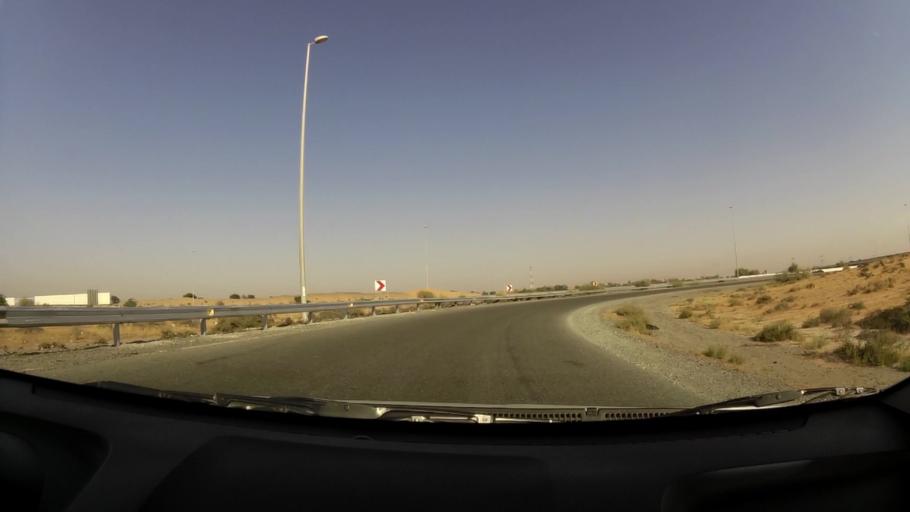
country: AE
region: Umm al Qaywayn
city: Umm al Qaywayn
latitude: 25.4549
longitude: 55.6157
